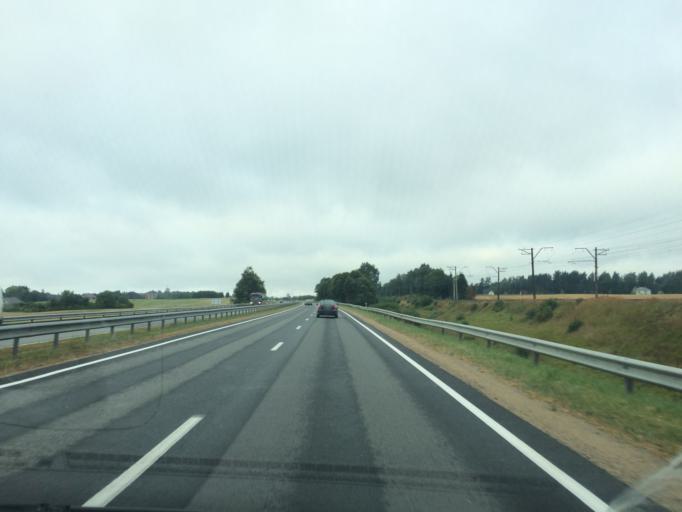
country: LV
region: Ikskile
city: Ikskile
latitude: 56.8469
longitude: 24.4596
